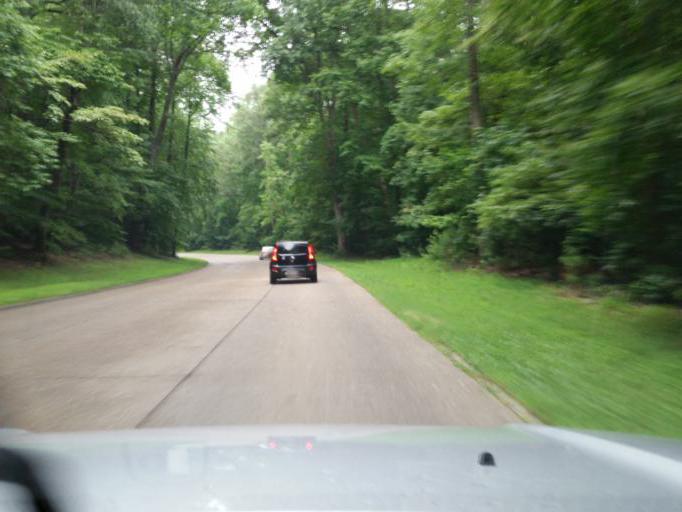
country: US
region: Virginia
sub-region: City of Williamsburg
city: Williamsburg
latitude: 37.2814
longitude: -76.6561
